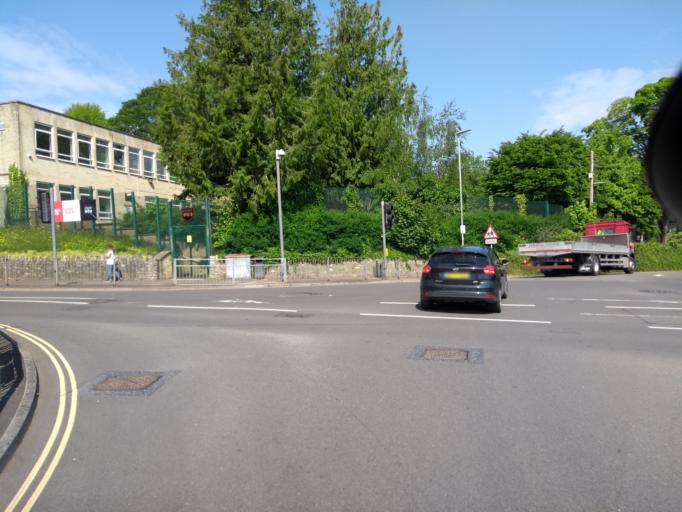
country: GB
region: England
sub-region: Somerset
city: Chard
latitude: 50.8736
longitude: -2.9599
